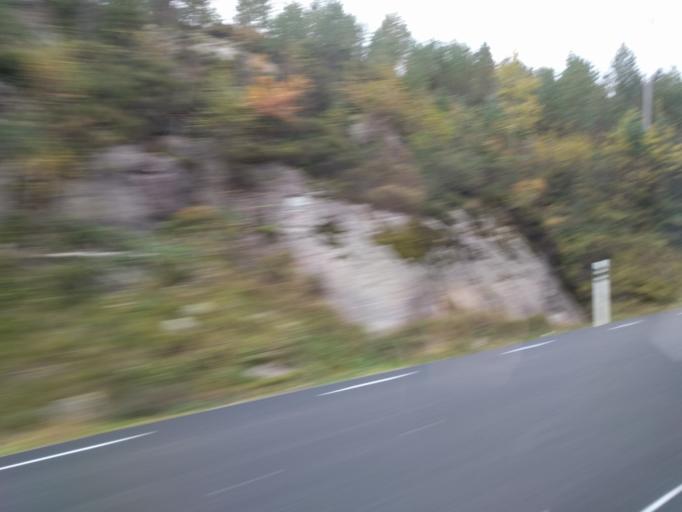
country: NO
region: Aust-Agder
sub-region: Iveland
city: Birketveit
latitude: 58.4377
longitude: 7.7870
